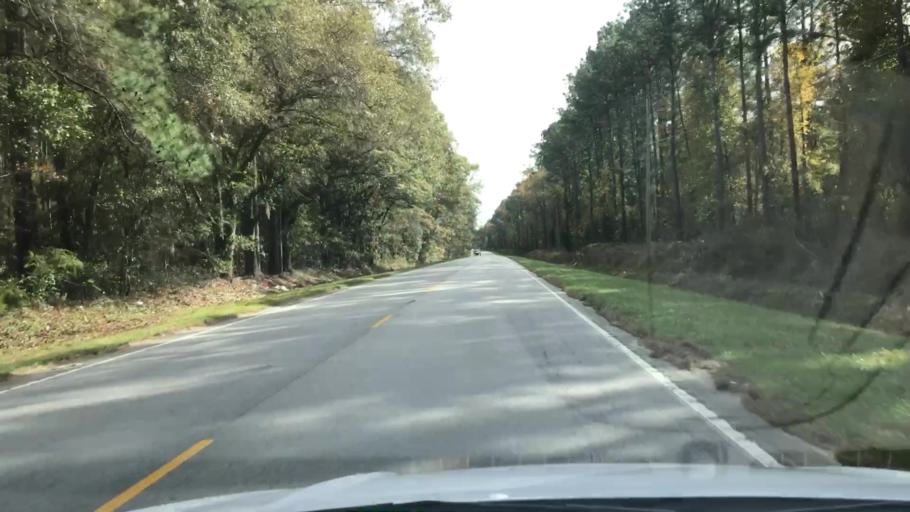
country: US
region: South Carolina
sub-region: Colleton County
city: Walterboro
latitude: 32.8012
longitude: -80.5029
